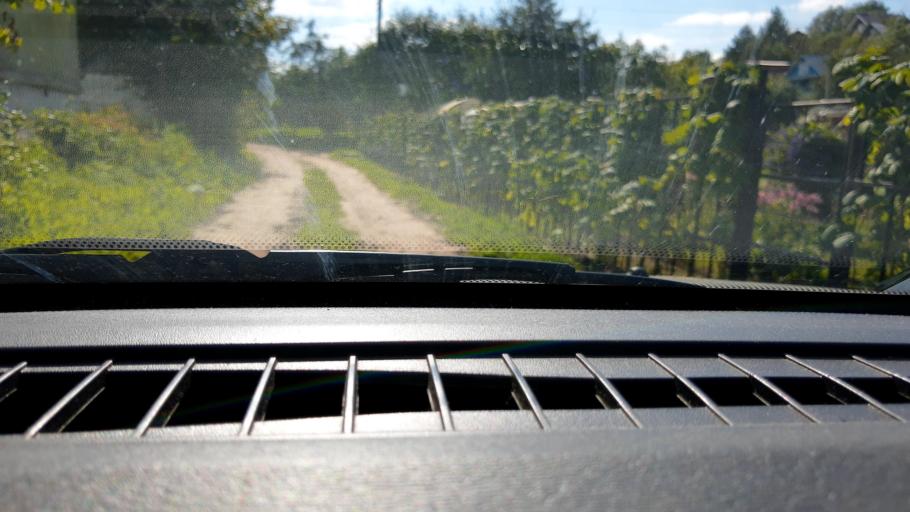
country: RU
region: Nizjnij Novgorod
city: Afonino
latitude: 56.2498
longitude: 44.0673
